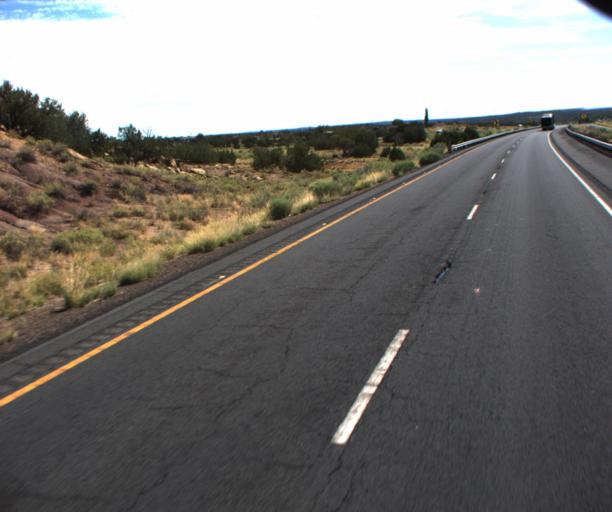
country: US
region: Arizona
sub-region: Apache County
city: Houck
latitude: 35.2817
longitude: -109.2389
